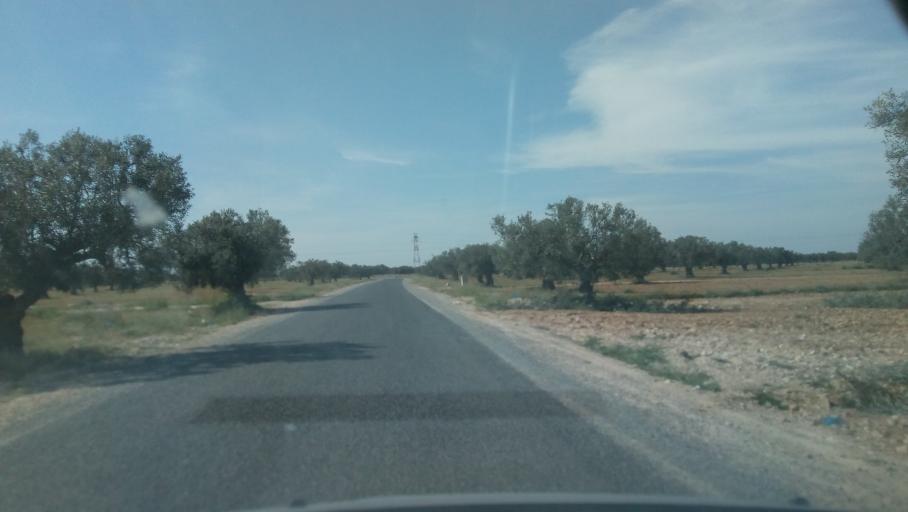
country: TN
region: Safaqis
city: Al Qarmadah
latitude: 34.8776
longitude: 10.8715
